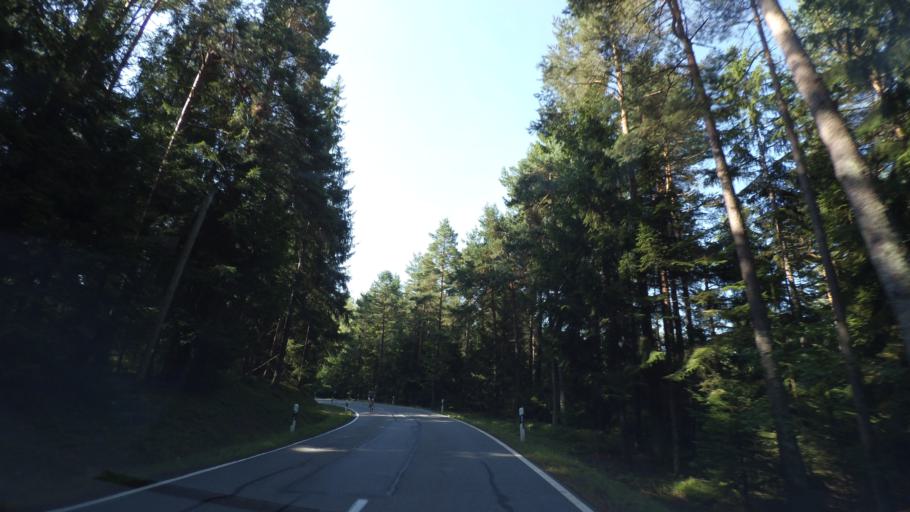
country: DE
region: Bavaria
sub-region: Lower Bavaria
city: Arnbruck
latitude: 49.1428
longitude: 13.0044
